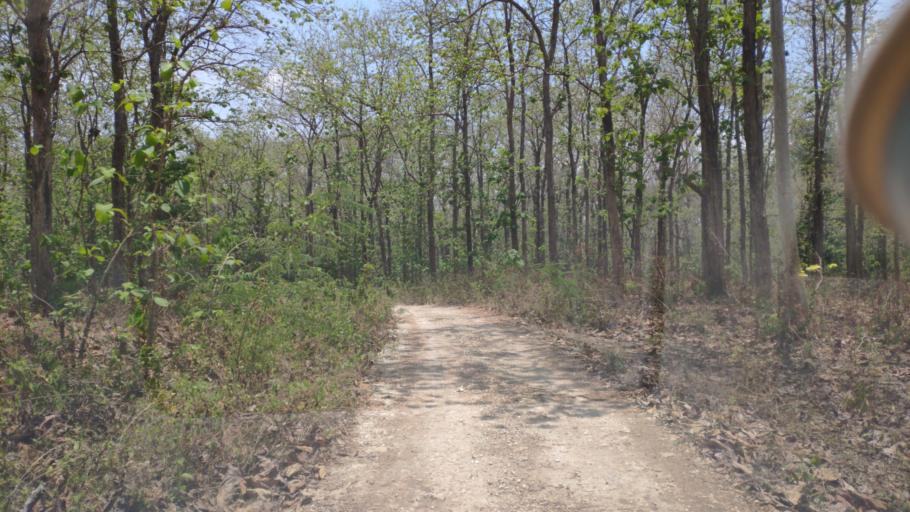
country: ID
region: Central Java
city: Botoh
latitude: -7.0742
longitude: 111.4836
